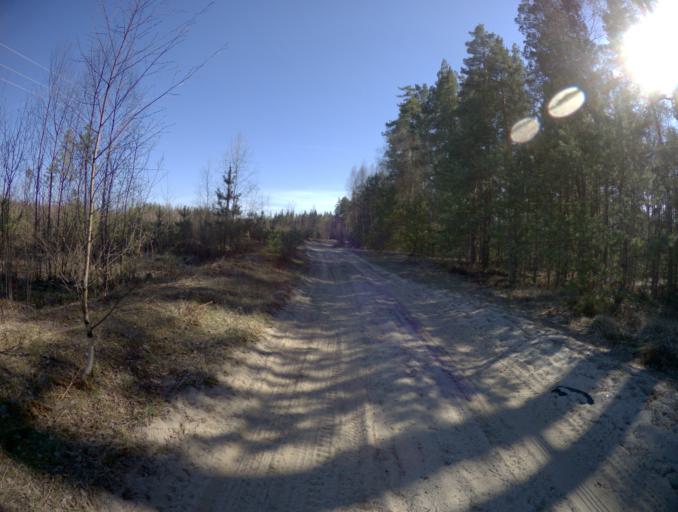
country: RU
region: Vladimir
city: Ivanishchi
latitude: 55.7628
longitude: 40.4071
